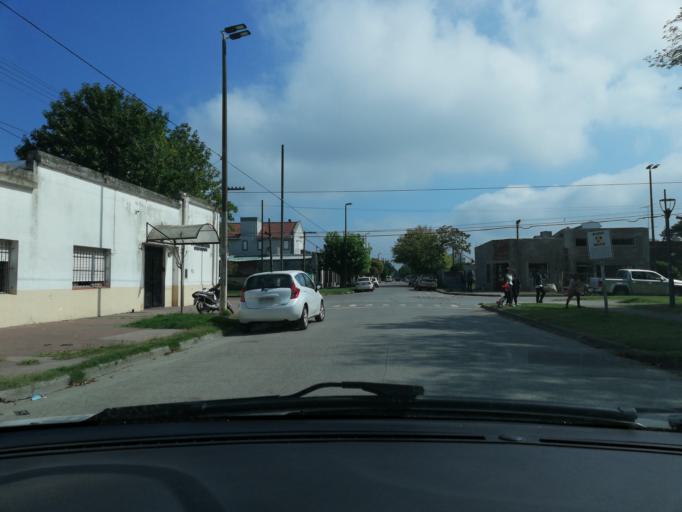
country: AR
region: Buenos Aires
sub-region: Partido de Balcarce
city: Balcarce
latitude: -37.8466
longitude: -58.2456
